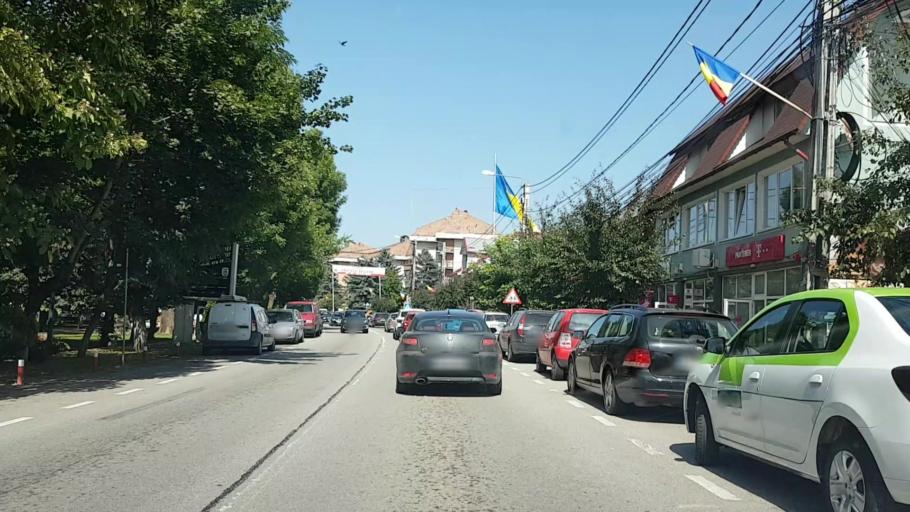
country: RO
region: Bistrita-Nasaud
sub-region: Comuna Beclean
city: Beclean
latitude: 47.1796
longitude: 24.1788
